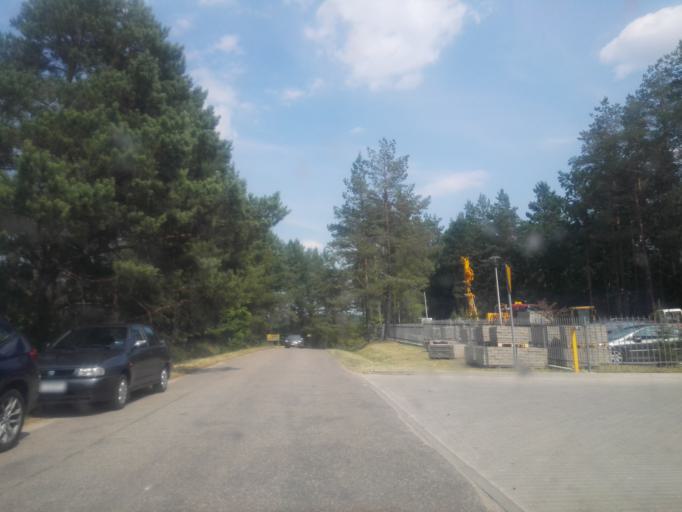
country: PL
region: Podlasie
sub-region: Suwalki
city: Suwalki
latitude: 54.0188
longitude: 23.0142
